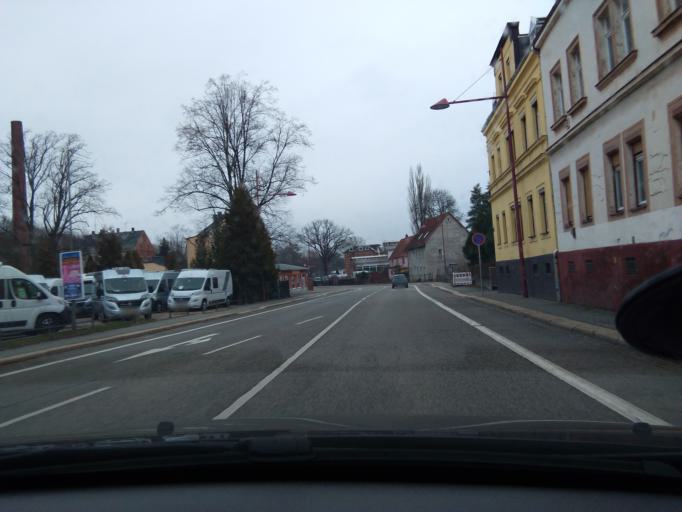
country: DE
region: Saxony
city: Wittgensdorf
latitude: 50.8329
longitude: 12.8764
